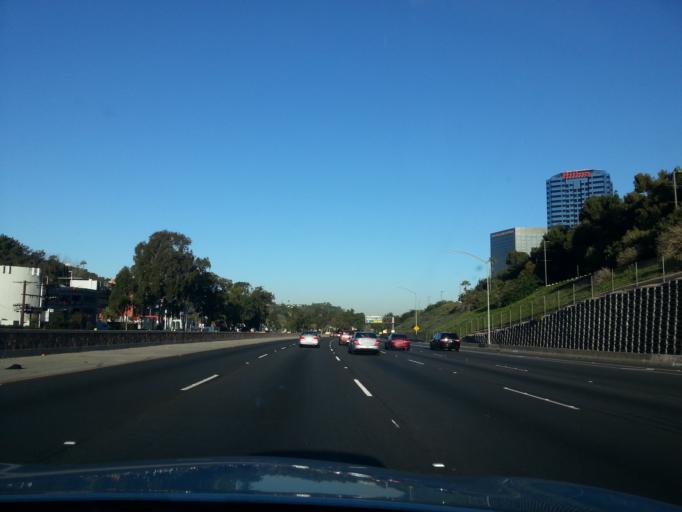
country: US
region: California
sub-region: Los Angeles County
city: Universal City
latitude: 34.1339
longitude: -118.3547
